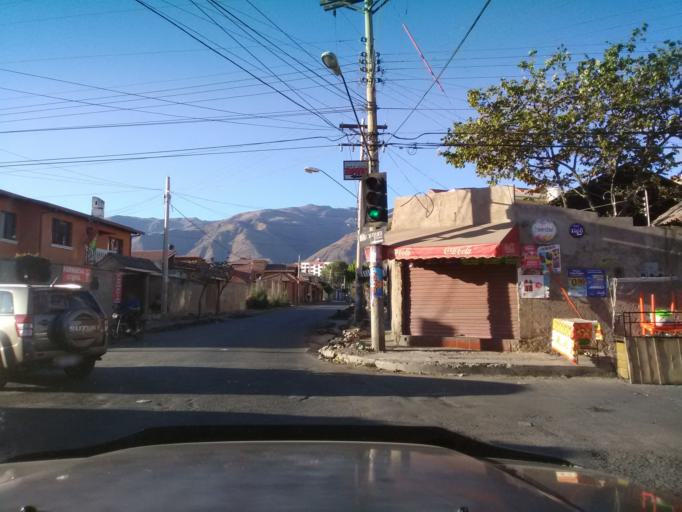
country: BO
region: Cochabamba
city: Cochabamba
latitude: -17.3700
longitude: -66.1886
